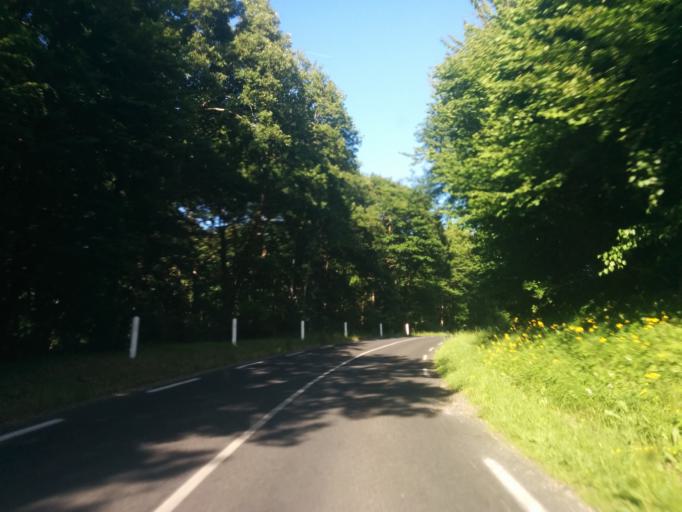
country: FR
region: Haute-Normandie
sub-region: Departement de l'Eure
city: Vernon
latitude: 49.0974
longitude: 1.5108
